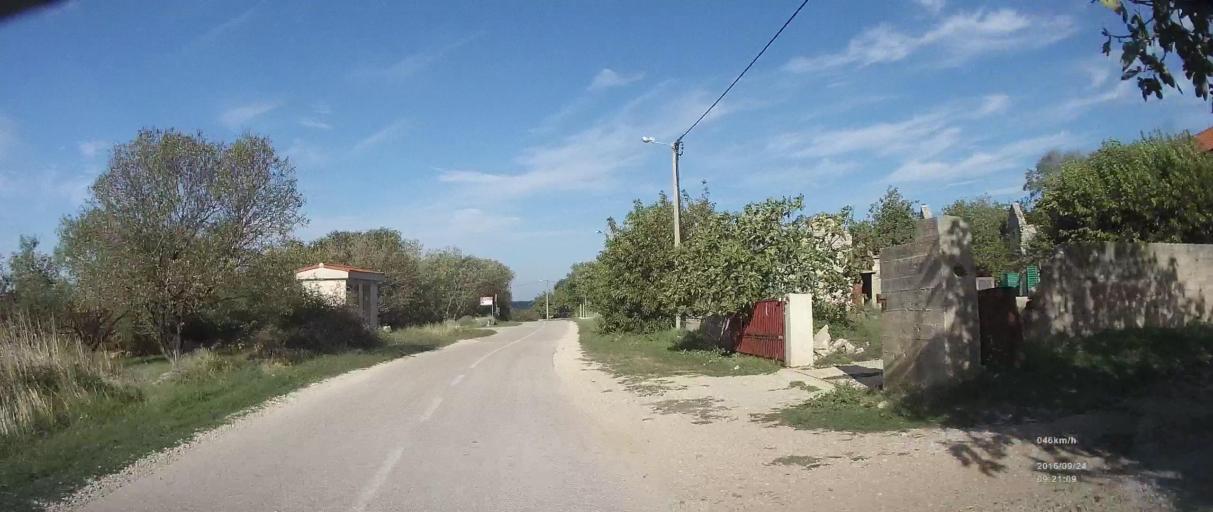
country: HR
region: Zadarska
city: Polaca
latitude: 44.0685
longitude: 15.4910
